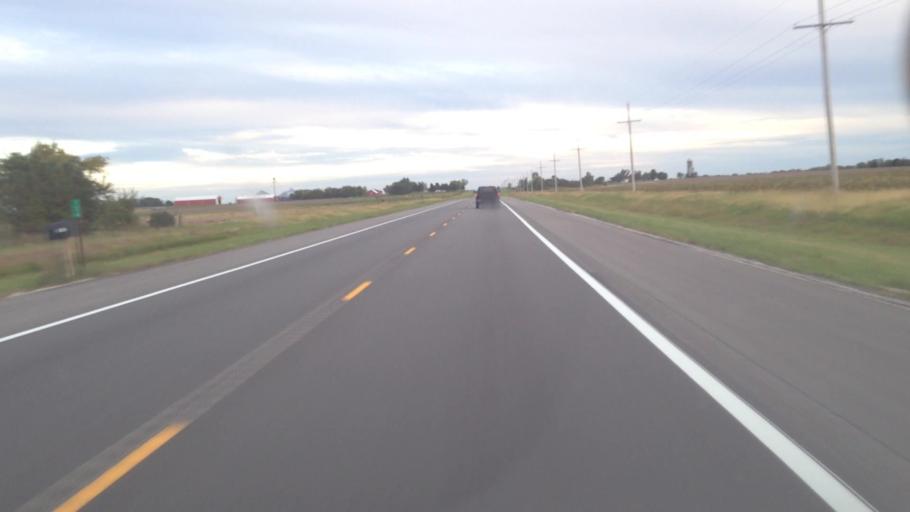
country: US
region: Kansas
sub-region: Franklin County
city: Ottawa
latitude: 38.5182
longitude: -95.2676
